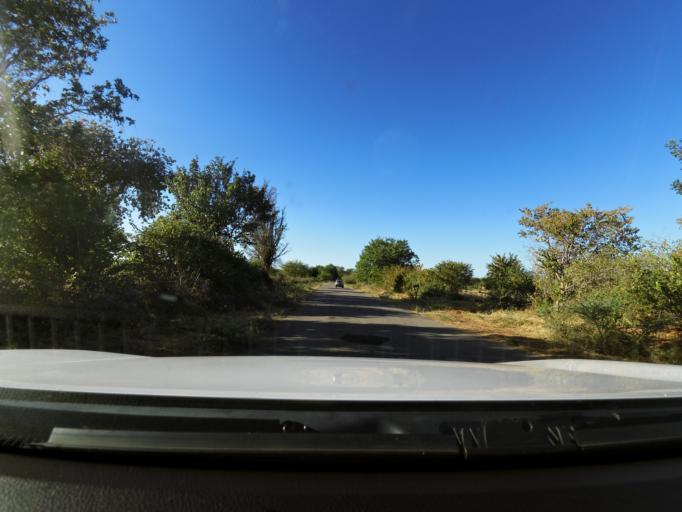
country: ZW
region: Matabeleland North
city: Kamativi Mine
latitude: -18.0511
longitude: 27.1089
